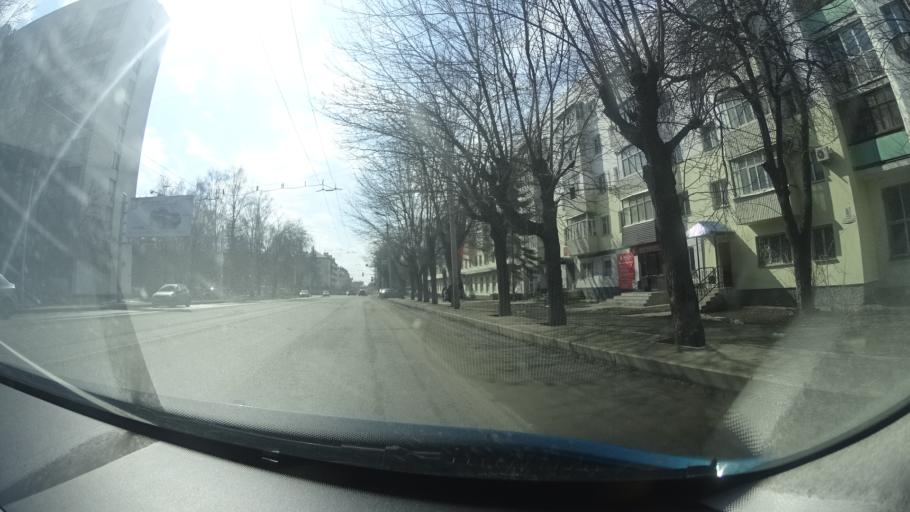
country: RU
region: Bashkortostan
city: Ufa
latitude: 54.7378
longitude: 55.9658
